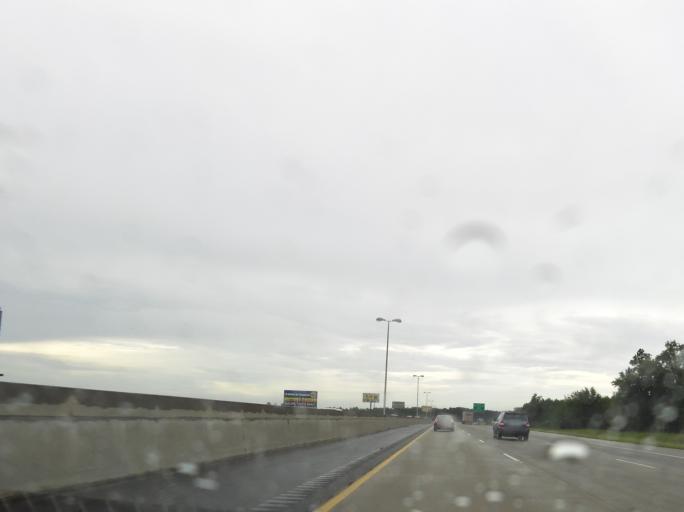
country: US
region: Georgia
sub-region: Cook County
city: Adel
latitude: 31.0634
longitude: -83.4011
